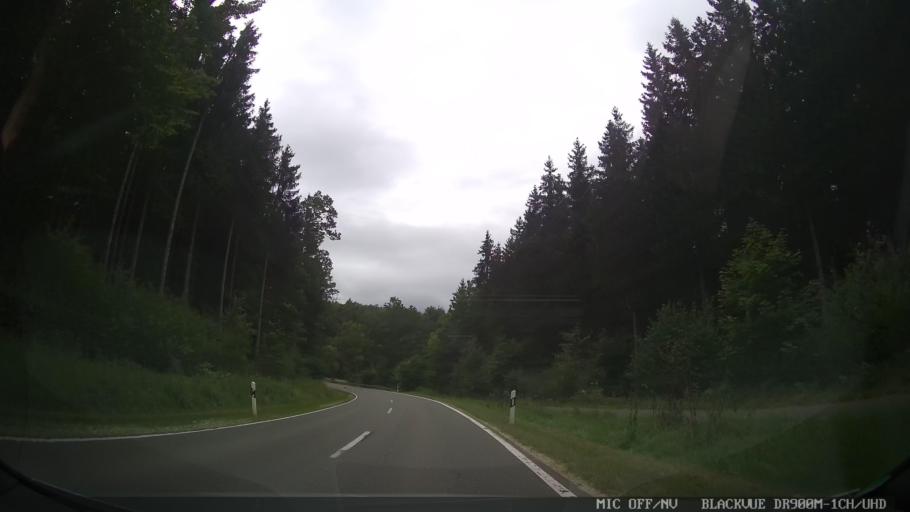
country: DE
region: Baden-Wuerttemberg
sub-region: Freiburg Region
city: Neuhausen ob Eck
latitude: 47.9549
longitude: 8.9360
